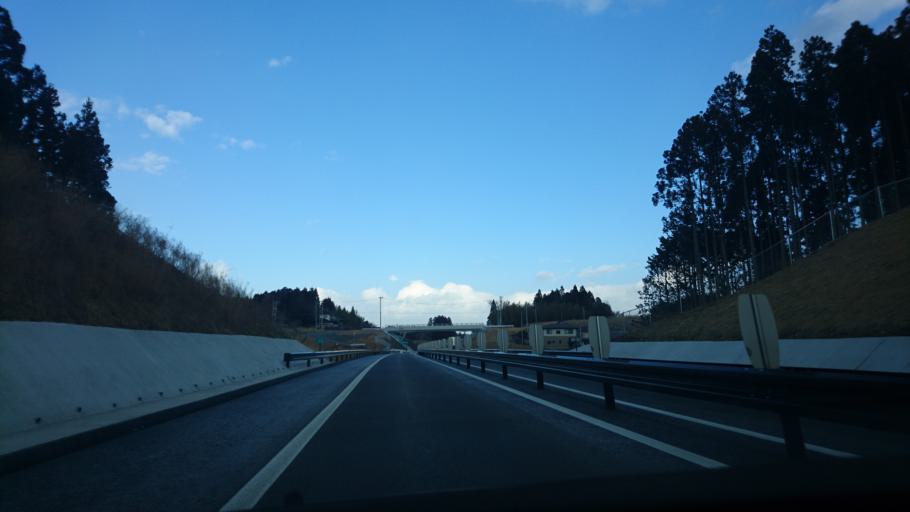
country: JP
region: Iwate
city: Ofunato
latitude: 38.7969
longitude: 141.5273
